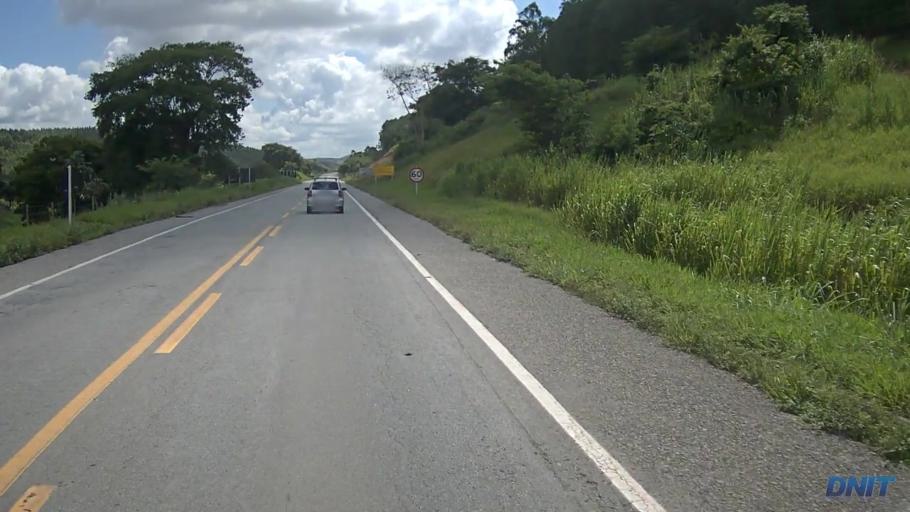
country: BR
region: Minas Gerais
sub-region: Governador Valadares
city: Governador Valadares
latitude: -19.0735
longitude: -42.1778
